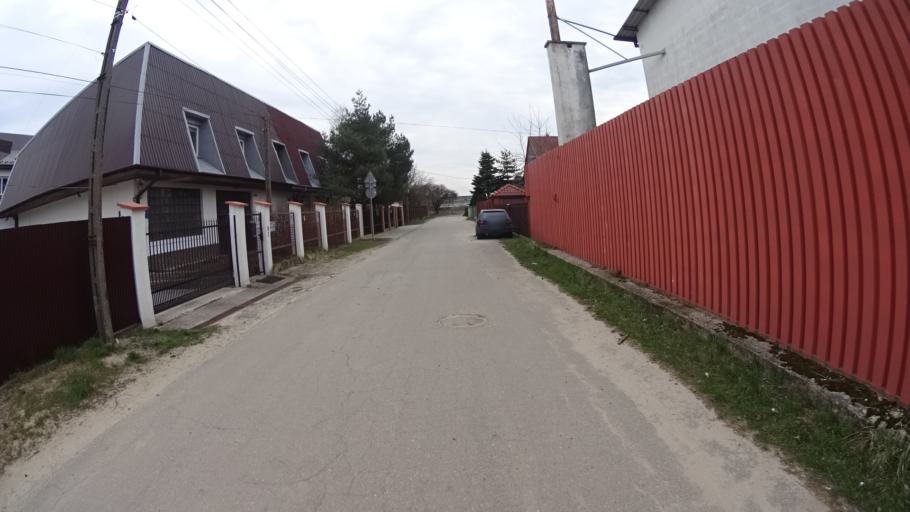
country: PL
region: Masovian Voivodeship
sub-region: Powiat warszawski zachodni
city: Ozarow Mazowiecki
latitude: 52.2089
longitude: 20.7886
